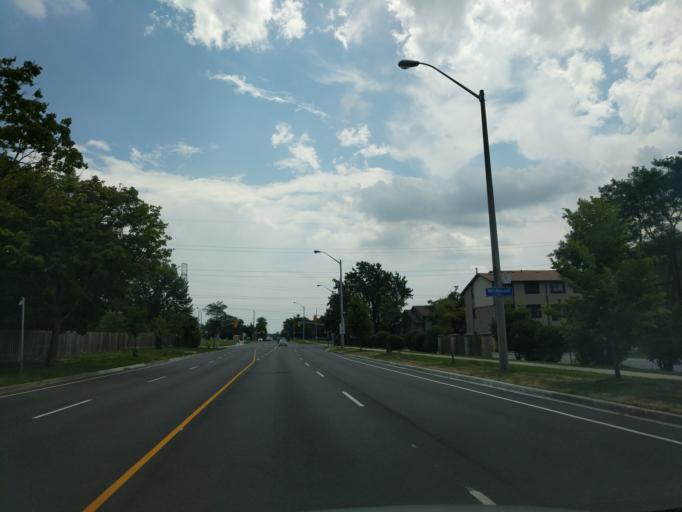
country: CA
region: Ontario
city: Scarborough
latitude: 43.8098
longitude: -79.3117
